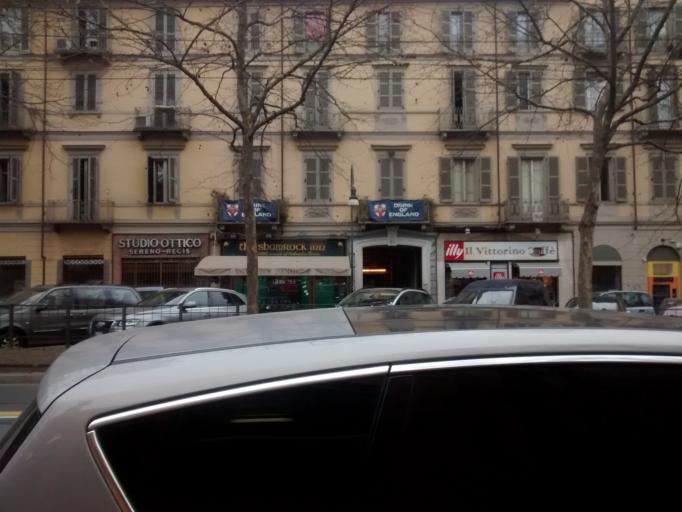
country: IT
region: Piedmont
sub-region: Provincia di Torino
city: Turin
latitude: 45.0609
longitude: 7.6844
